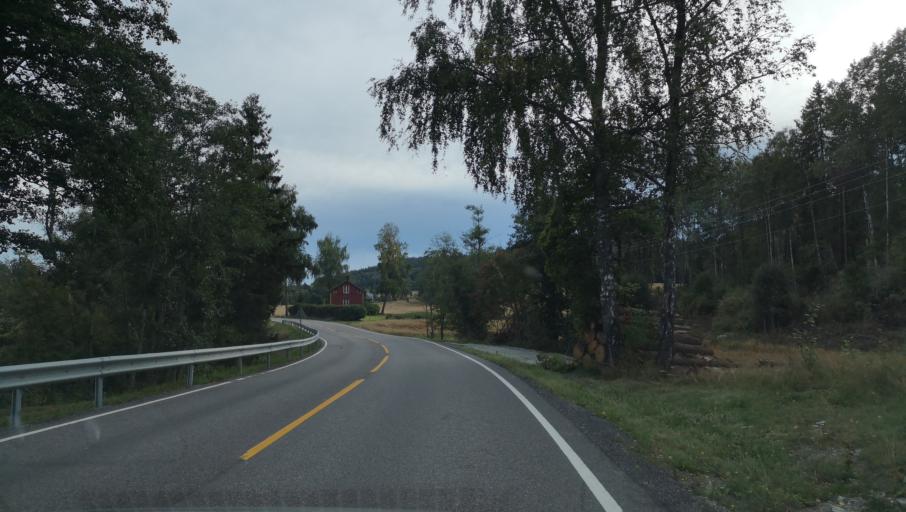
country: NO
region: Ostfold
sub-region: Hobol
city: Tomter
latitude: 59.6986
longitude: 11.0426
